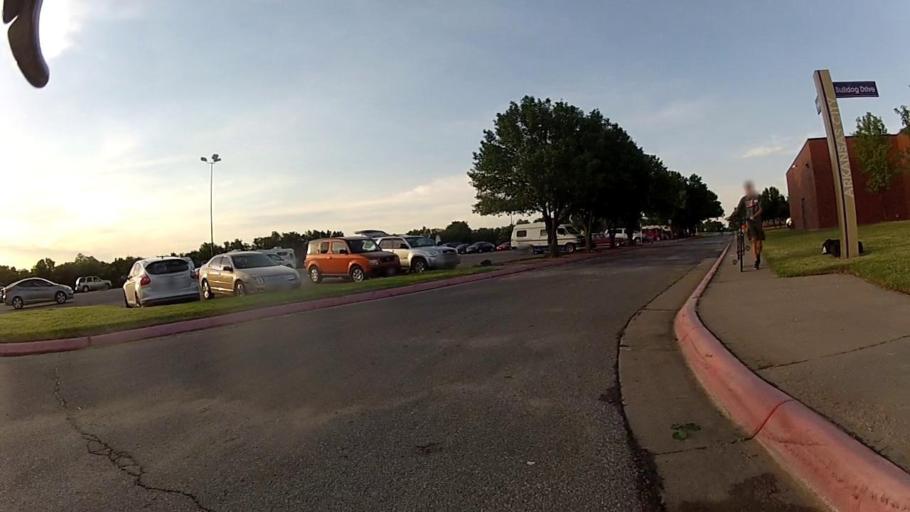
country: US
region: Kansas
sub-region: Cowley County
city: Arkansas City
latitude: 37.0870
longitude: -97.0528
